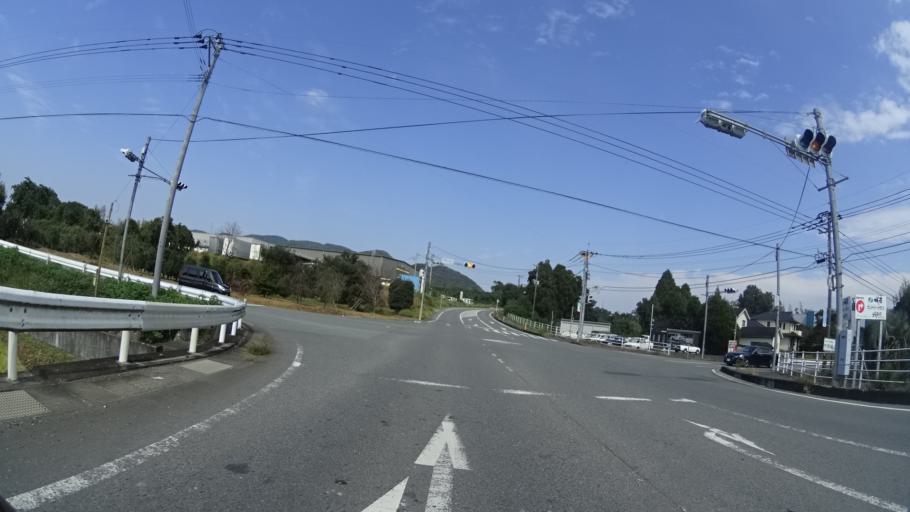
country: JP
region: Kumamoto
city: Matsubase
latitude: 32.6665
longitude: 130.7186
